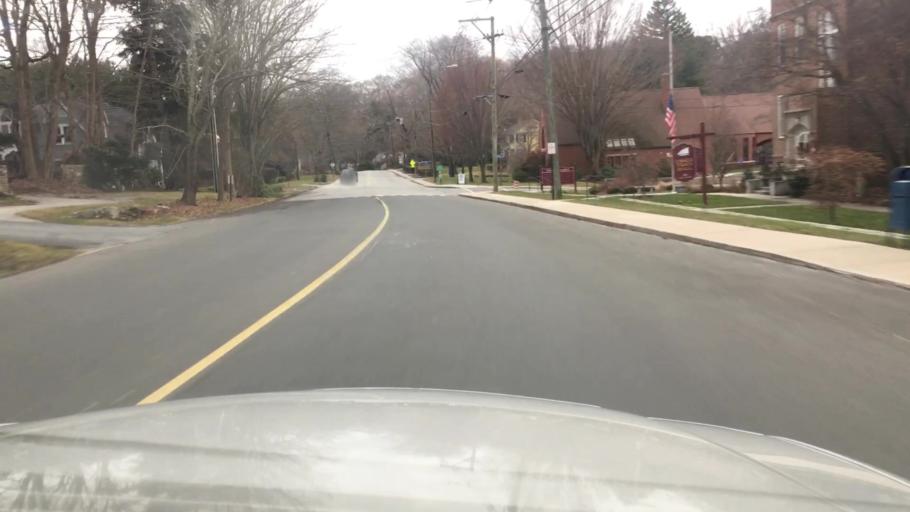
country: US
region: Connecticut
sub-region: Middlesex County
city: Essex Village
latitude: 41.3538
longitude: -72.3955
